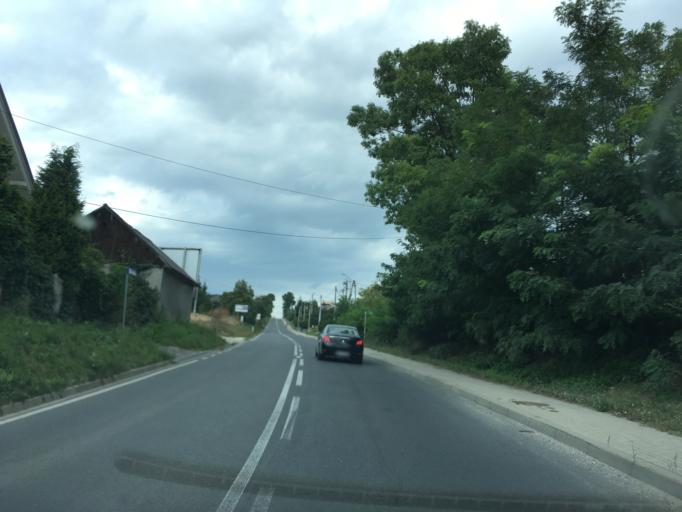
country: PL
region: Lesser Poland Voivodeship
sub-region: Powiat krakowski
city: Giebultow
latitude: 50.1664
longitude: 19.8996
